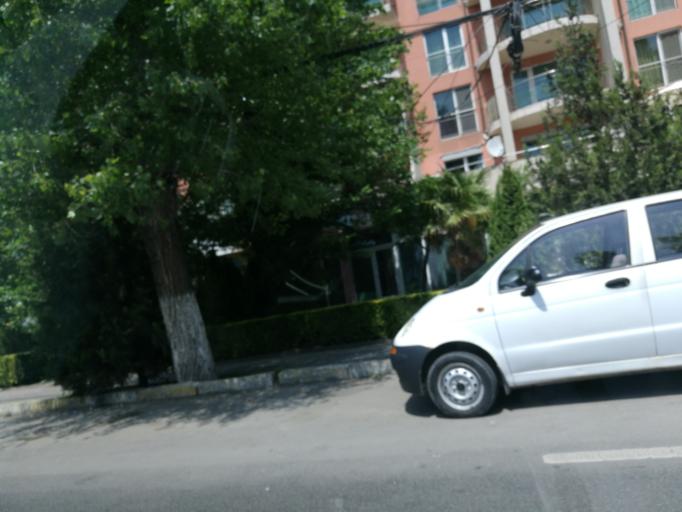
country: RO
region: Constanta
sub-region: Municipiul Constanta
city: Palazu Mare
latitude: 44.2182
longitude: 28.6351
